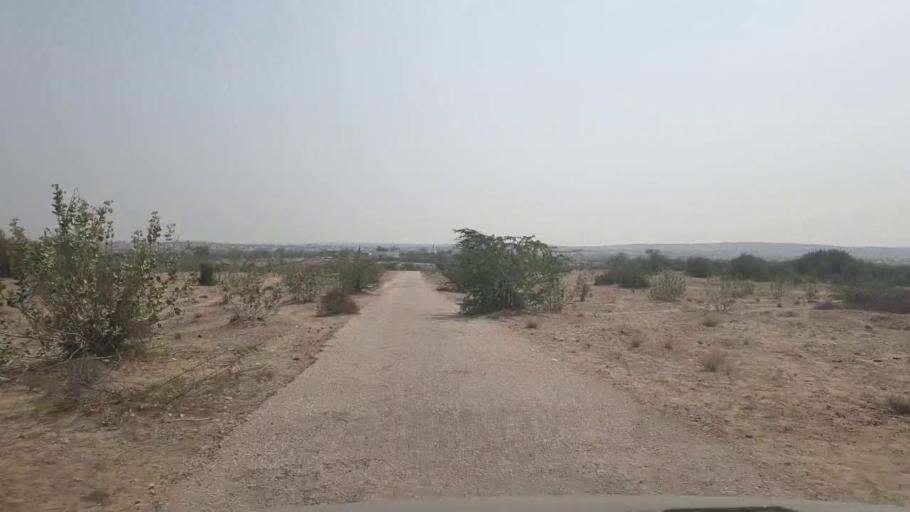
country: PK
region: Sindh
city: Chor
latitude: 25.4605
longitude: 69.7844
